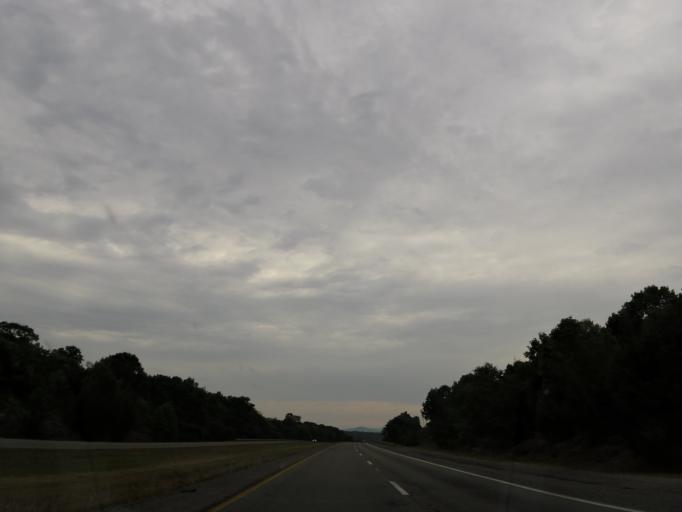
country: US
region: Alabama
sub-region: Jackson County
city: Scottsboro
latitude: 34.6176
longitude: -86.2130
